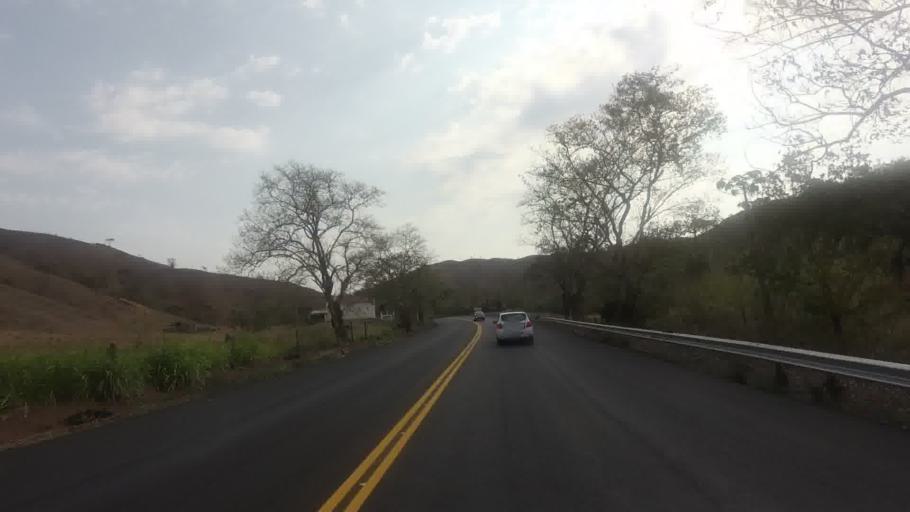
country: BR
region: Rio de Janeiro
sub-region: Bom Jesus Do Itabapoana
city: Bom Jesus do Itabapoana
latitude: -21.2128
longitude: -41.7333
